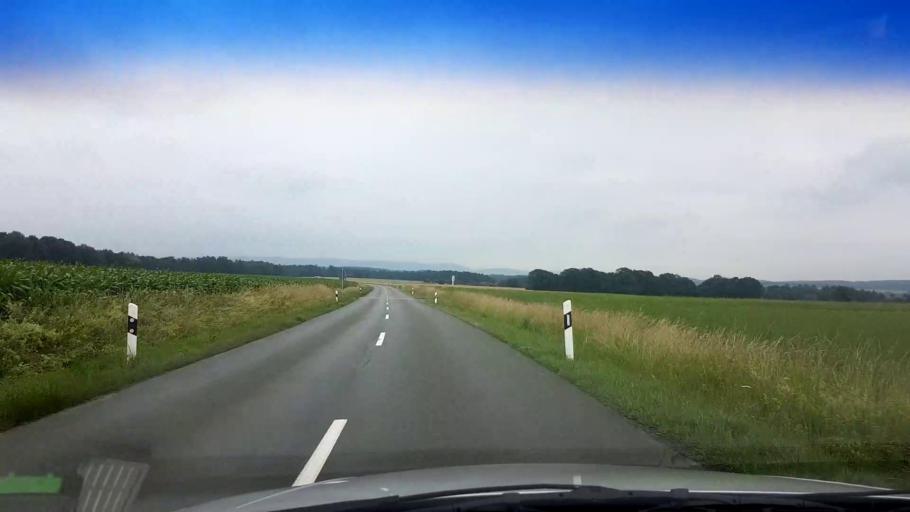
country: DE
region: Bavaria
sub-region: Upper Franconia
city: Weismain
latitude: 50.0824
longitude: 11.3034
